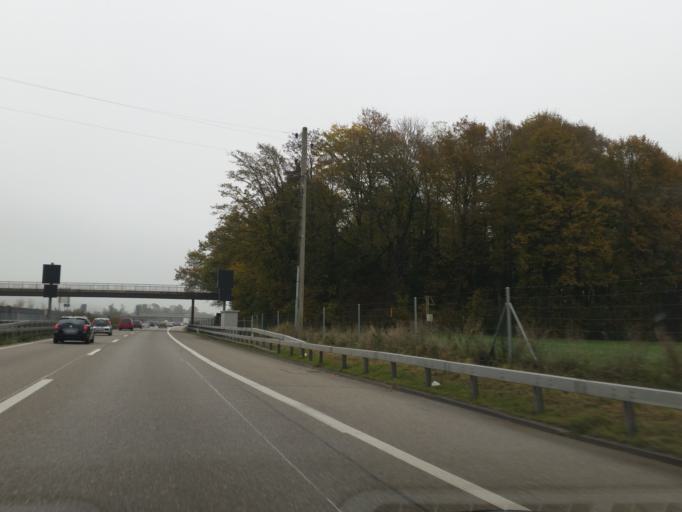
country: CH
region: Solothurn
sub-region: Bezirk Gaeu
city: Oensingen
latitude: 47.2853
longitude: 7.7271
